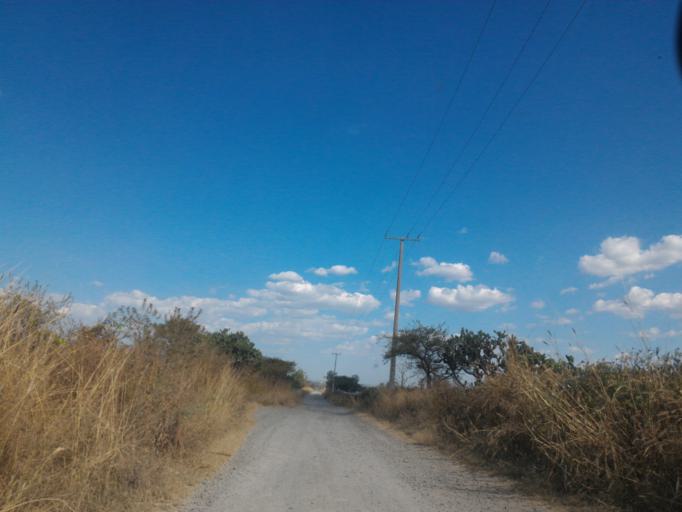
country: MX
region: Jalisco
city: San Diego de Alejandria
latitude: 20.8844
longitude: -101.9968
